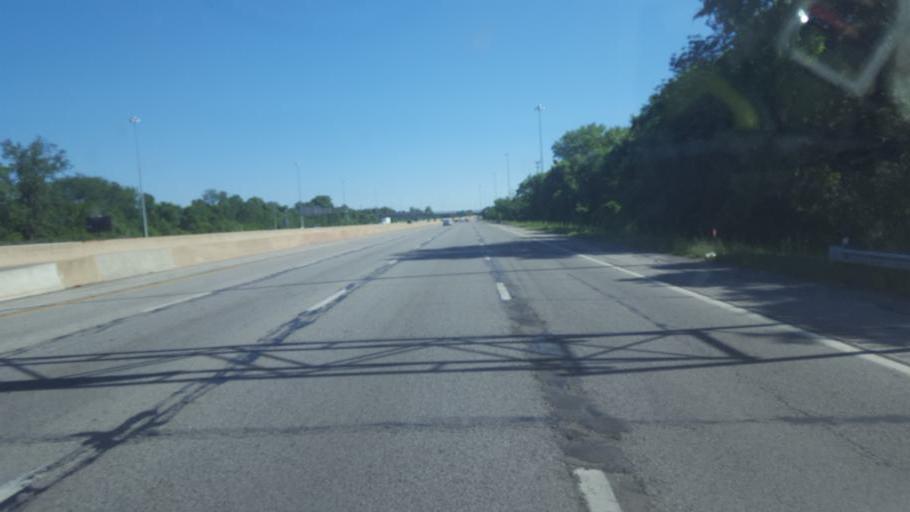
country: US
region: Ohio
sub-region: Franklin County
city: Reynoldsburg
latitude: 39.9488
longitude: -82.8459
